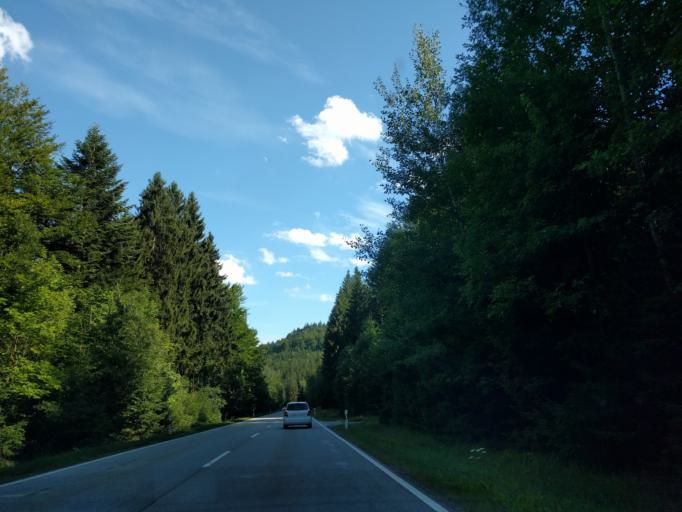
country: DE
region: Bavaria
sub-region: Lower Bavaria
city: Langdorf
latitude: 49.0261
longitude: 13.1293
